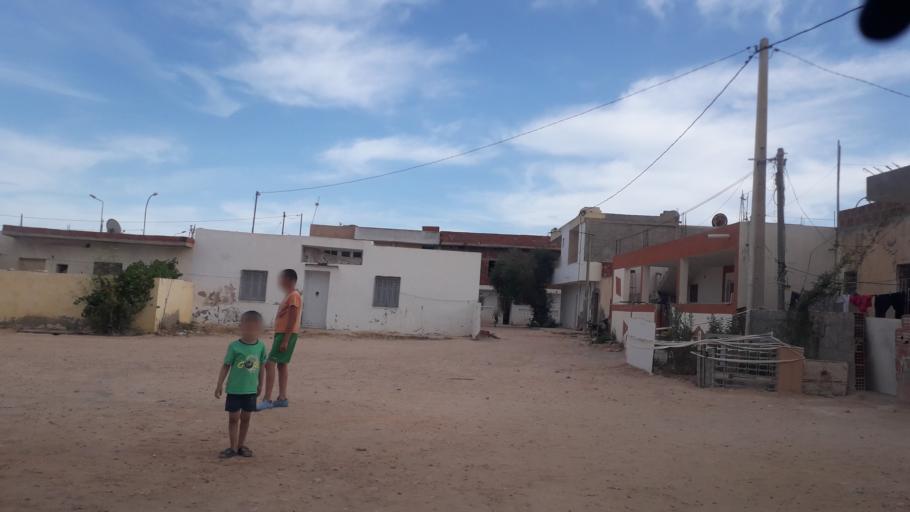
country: TN
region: Safaqis
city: Al Qarmadah
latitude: 34.8867
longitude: 10.7591
